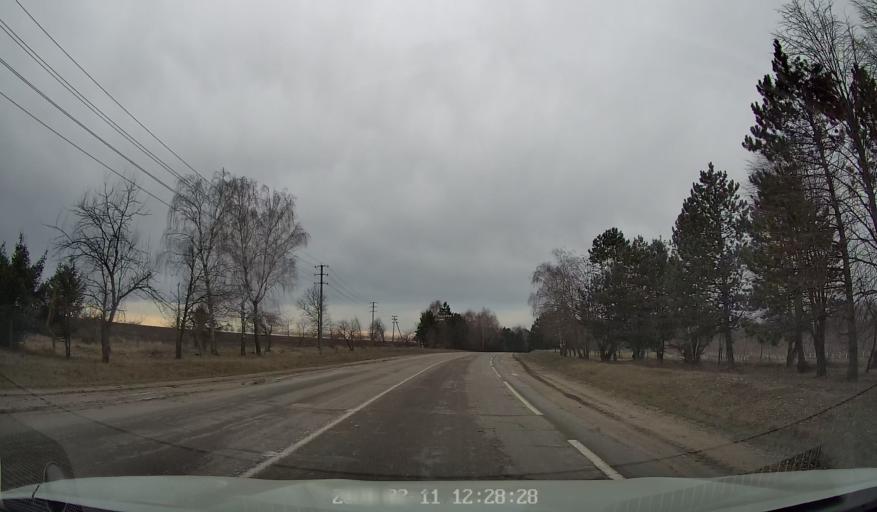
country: MD
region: Raionul Edinet
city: Edinet
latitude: 48.1446
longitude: 27.3010
